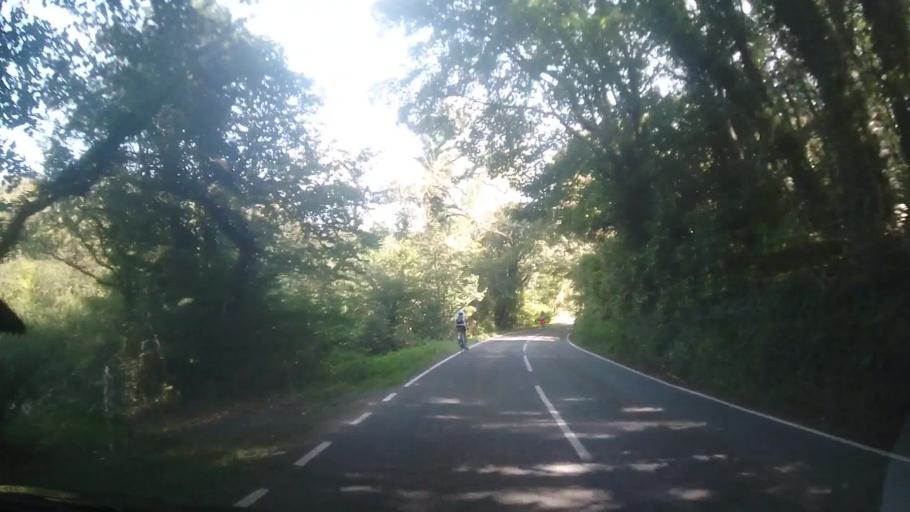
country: GB
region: Wales
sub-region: Pembrokeshire
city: Scleddau
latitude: 51.9364
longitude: -5.0178
